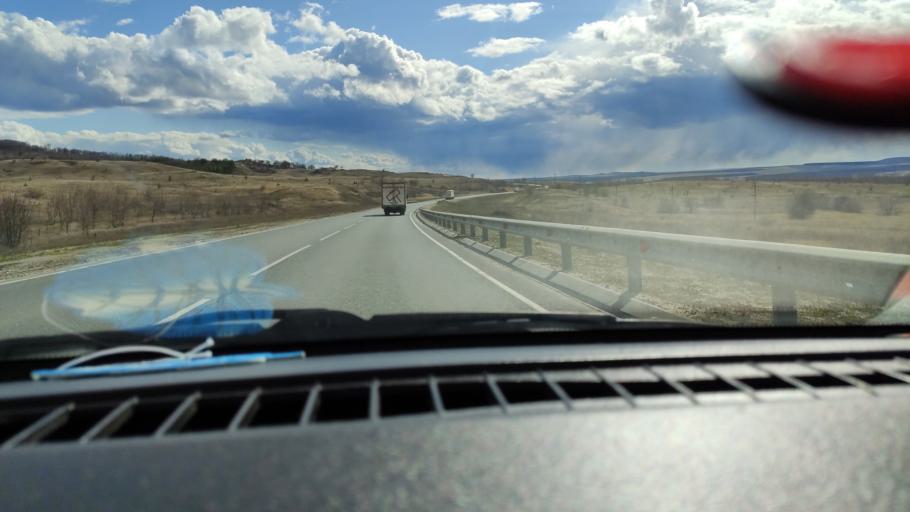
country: RU
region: Saratov
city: Alekseyevka
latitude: 52.3346
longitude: 47.9275
